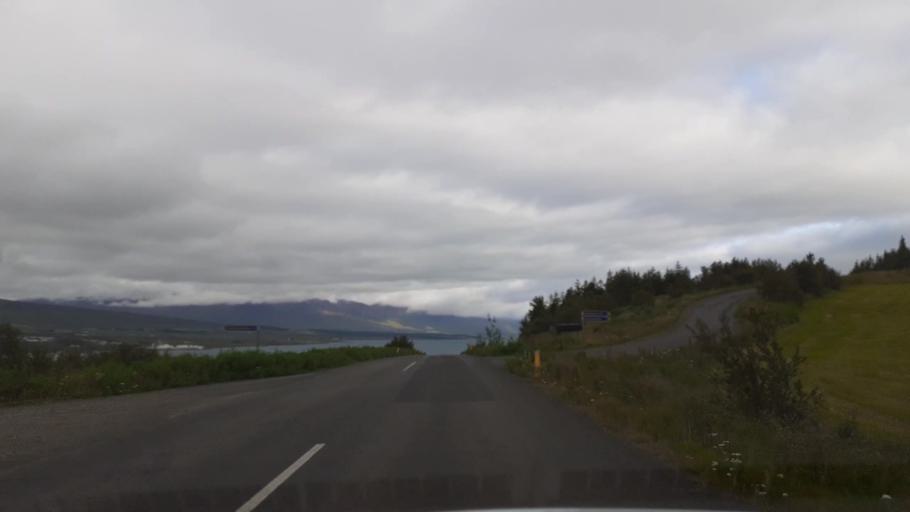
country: IS
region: Northeast
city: Akureyri
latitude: 65.6841
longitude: -18.0449
